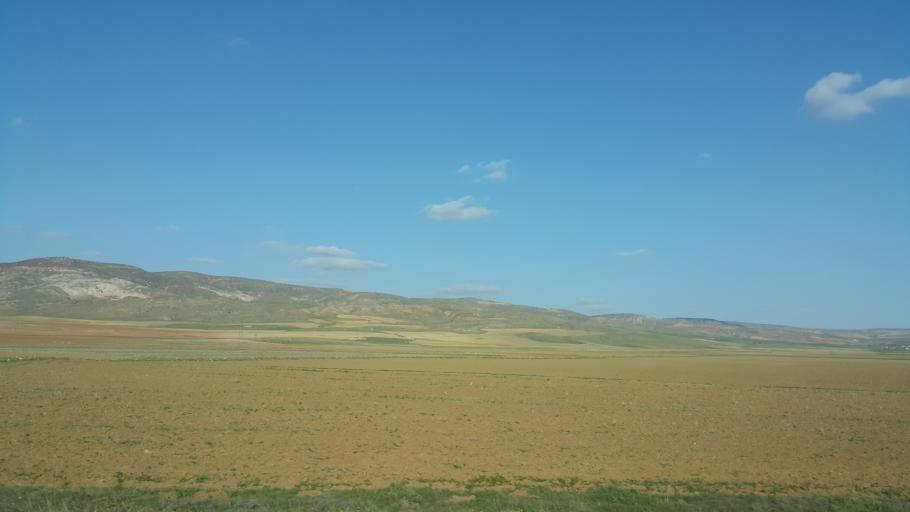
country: TR
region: Ankara
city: Sereflikochisar
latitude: 38.8780
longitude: 33.5879
